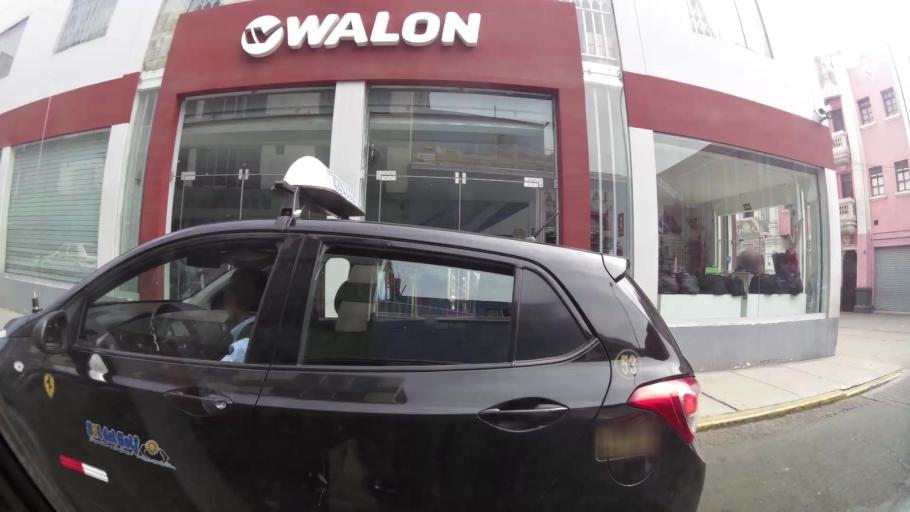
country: PE
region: La Libertad
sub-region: Provincia de Trujillo
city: Trujillo
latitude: -8.1085
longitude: -79.0248
